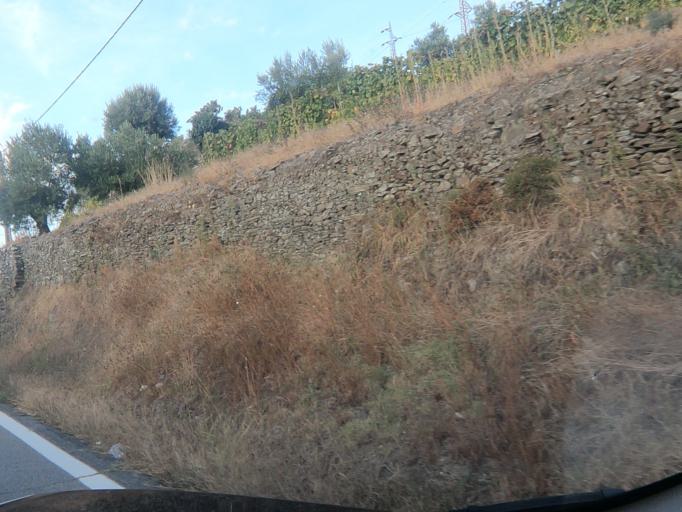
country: PT
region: Vila Real
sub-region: Peso da Regua
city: Peso da Regua
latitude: 41.1785
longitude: -7.7765
